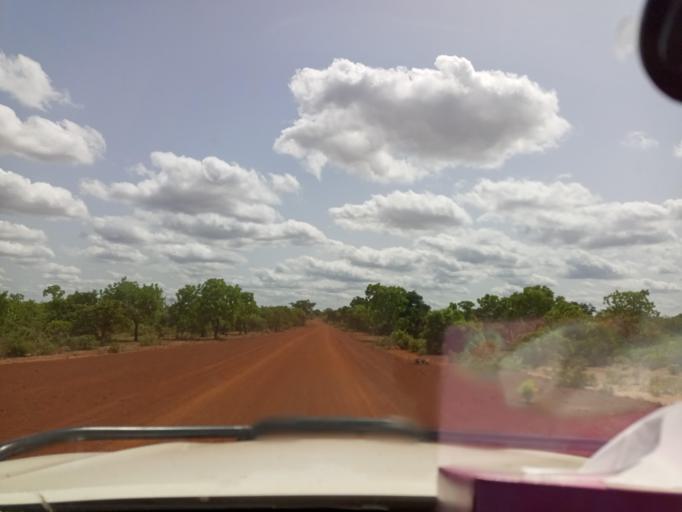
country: ML
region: Sikasso
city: Kolondieba
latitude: 11.5760
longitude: -6.6897
